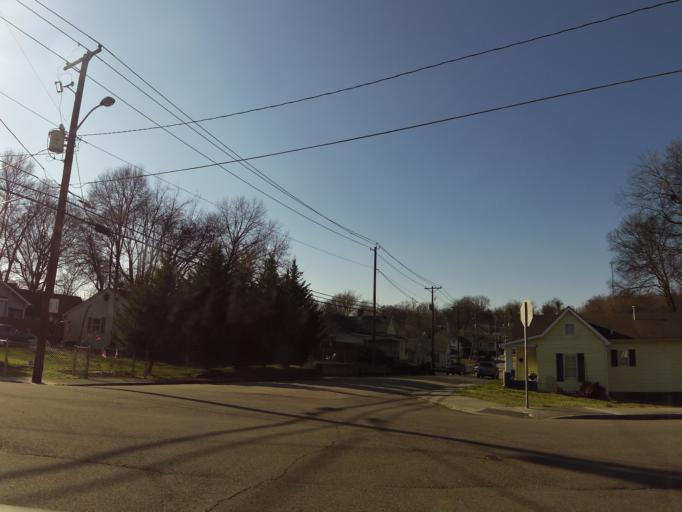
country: US
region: Tennessee
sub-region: Knox County
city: Knoxville
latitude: 35.9697
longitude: -83.9330
